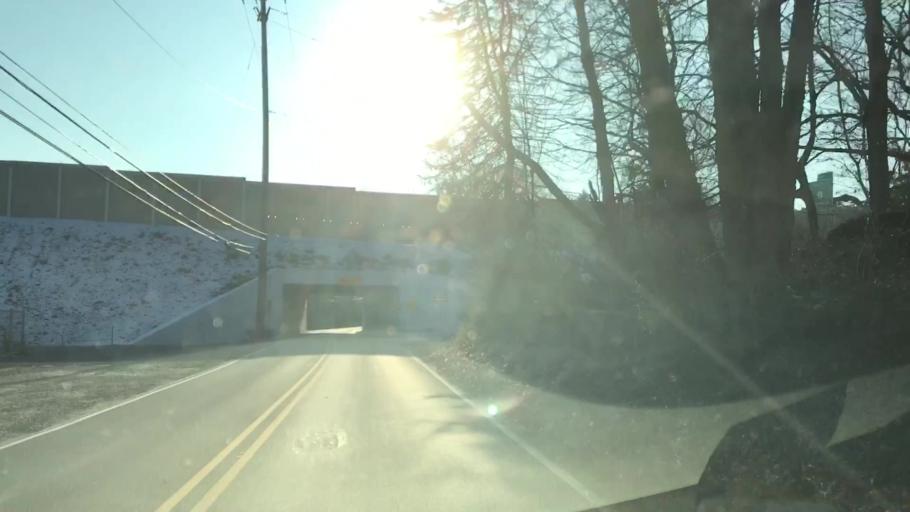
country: US
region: Pennsylvania
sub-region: Allegheny County
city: Gibsonia
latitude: 40.6081
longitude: -79.9422
